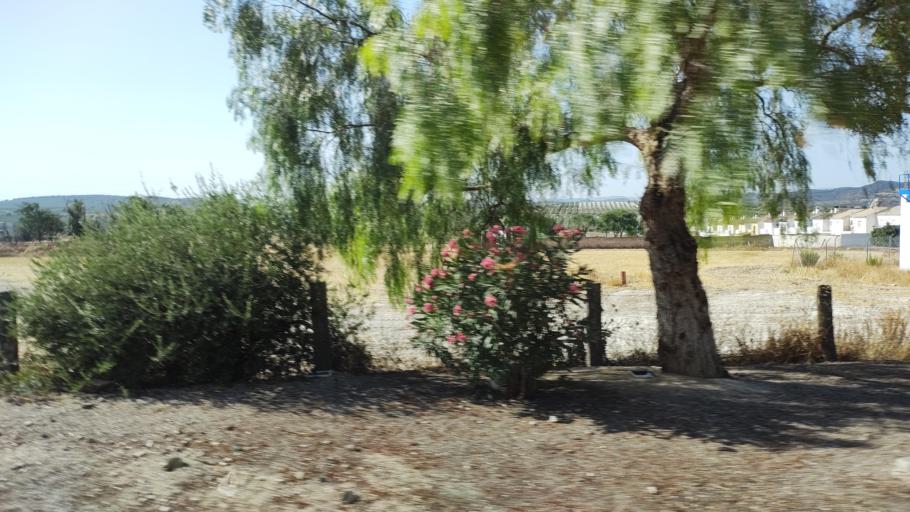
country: ES
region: Andalusia
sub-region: Provincia de Sevilla
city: Aguadulce
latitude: 37.2563
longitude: -4.9853
